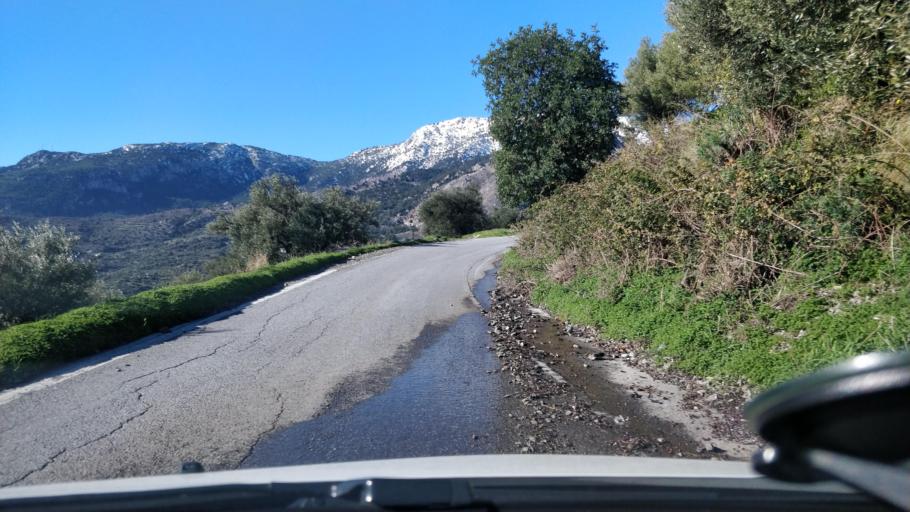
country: GR
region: Crete
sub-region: Nomos Lasithiou
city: Kritsa
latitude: 35.0782
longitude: 25.5823
